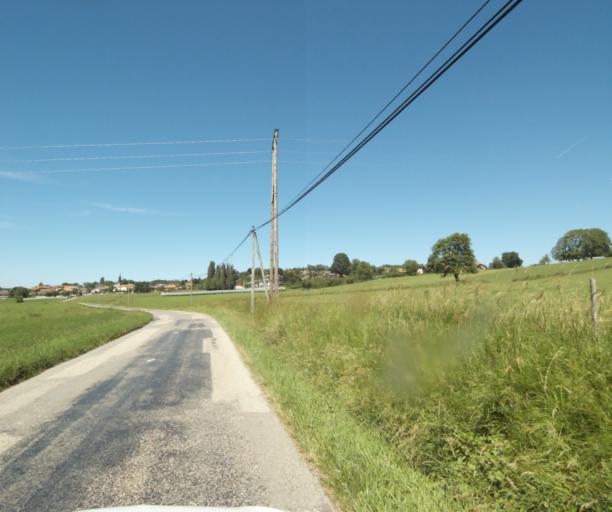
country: FR
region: Rhone-Alpes
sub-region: Departement de la Haute-Savoie
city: Ballaison
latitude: 46.2933
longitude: 6.3263
